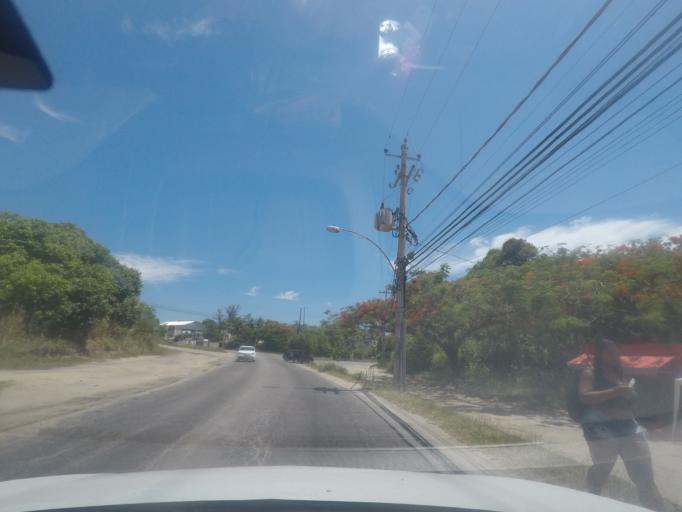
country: BR
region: Rio de Janeiro
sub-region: Itaguai
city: Itaguai
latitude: -22.9969
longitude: -43.6503
